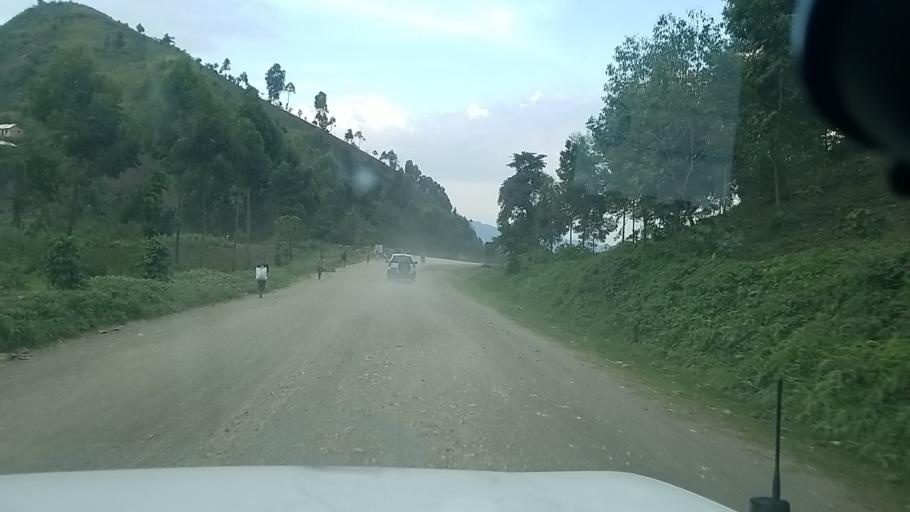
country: CD
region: Nord Kivu
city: Sake
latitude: -1.5706
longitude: 29.0460
